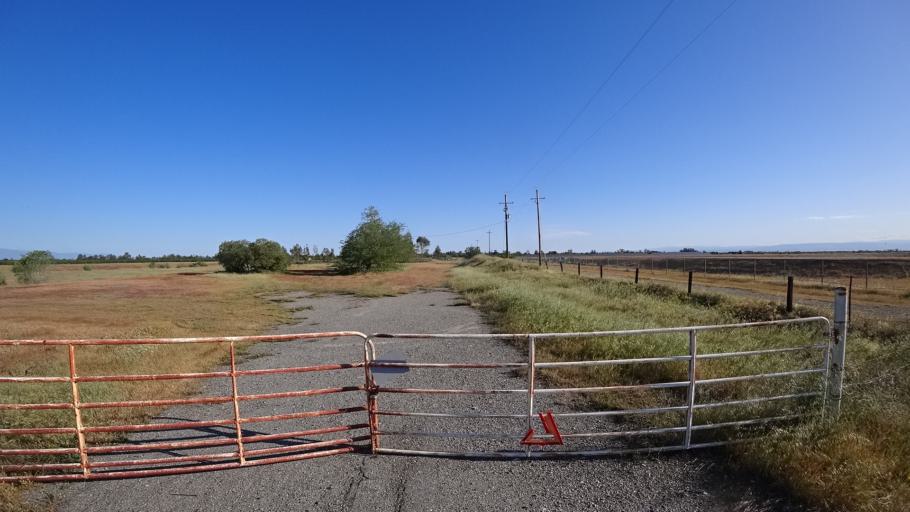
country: US
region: California
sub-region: Glenn County
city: Orland
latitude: 39.7180
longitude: -122.1597
